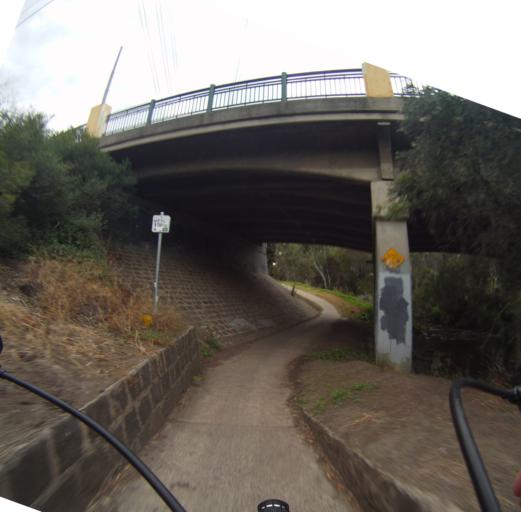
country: AU
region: Victoria
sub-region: Moreland
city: Coburg
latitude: -37.7574
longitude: 144.9801
